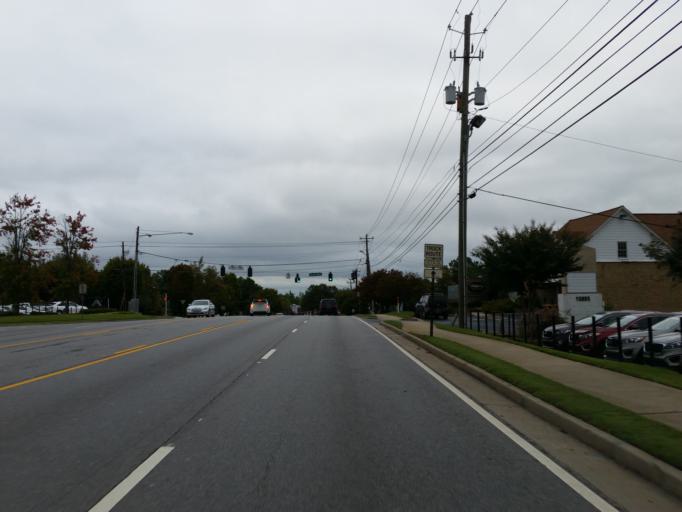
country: US
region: Georgia
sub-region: Fulton County
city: Roswell
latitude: 34.0455
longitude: -84.3401
